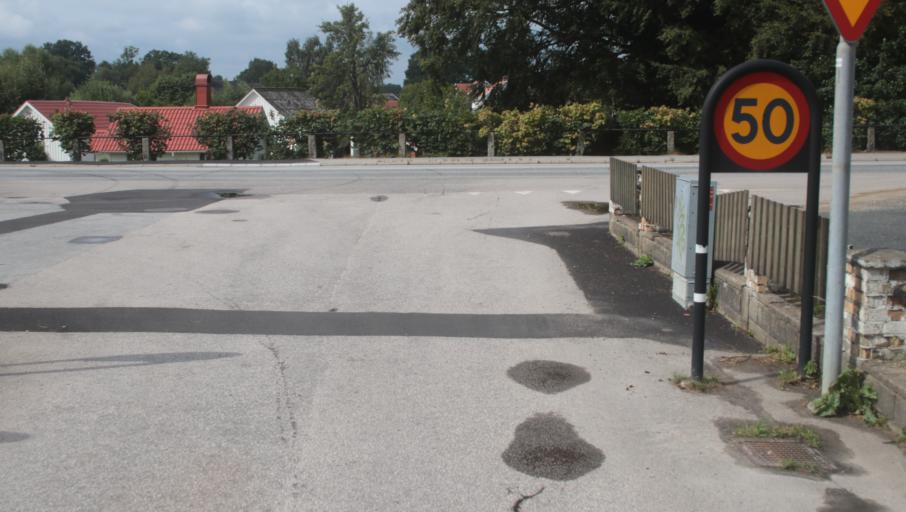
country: SE
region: Blekinge
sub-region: Karlshamns Kommun
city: Karlshamn
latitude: 56.2132
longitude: 14.8432
